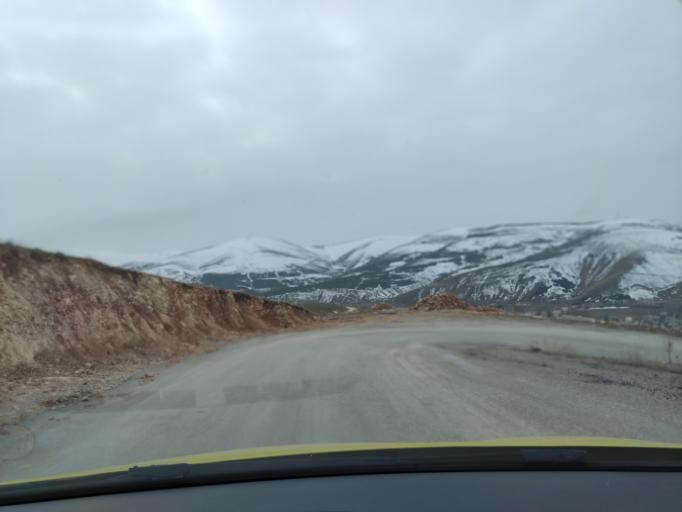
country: TR
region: Bayburt
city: Bayburt
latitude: 40.2579
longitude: 40.2378
